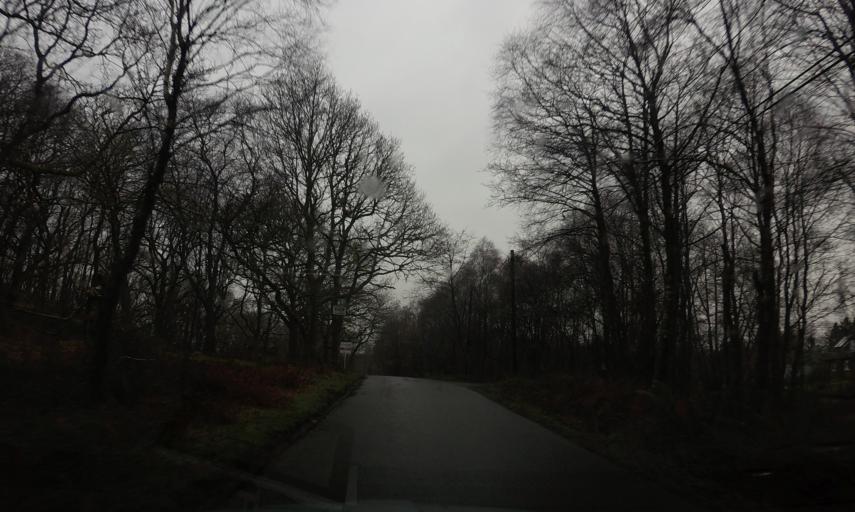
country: GB
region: Scotland
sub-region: West Dunbartonshire
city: Balloch
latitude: 56.1223
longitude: -4.5961
